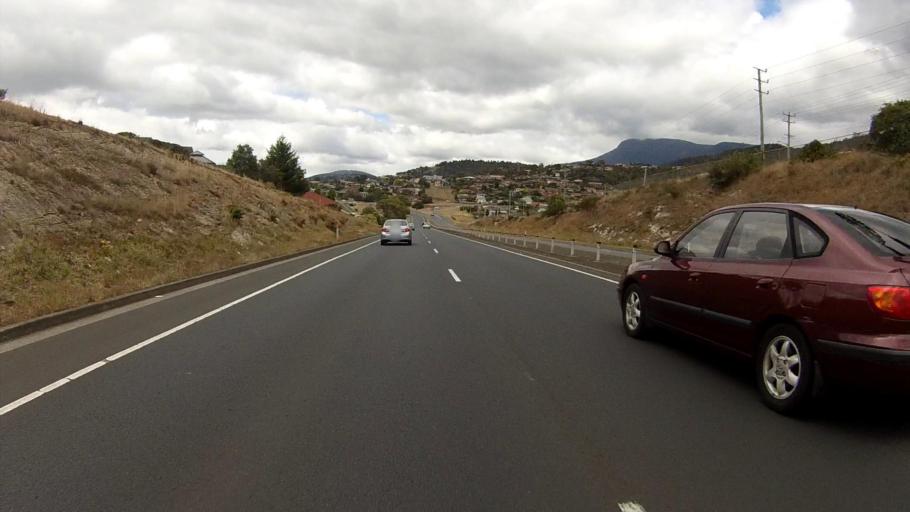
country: AU
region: Tasmania
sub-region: Glenorchy
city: Berriedale
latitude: -42.8106
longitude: 147.2501
